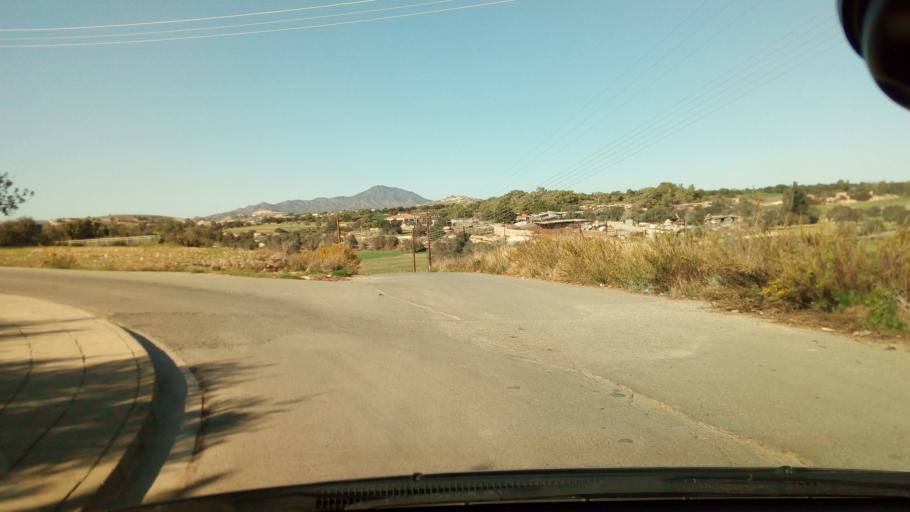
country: CY
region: Larnaka
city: Tersefanou
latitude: 34.8081
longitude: 33.4928
